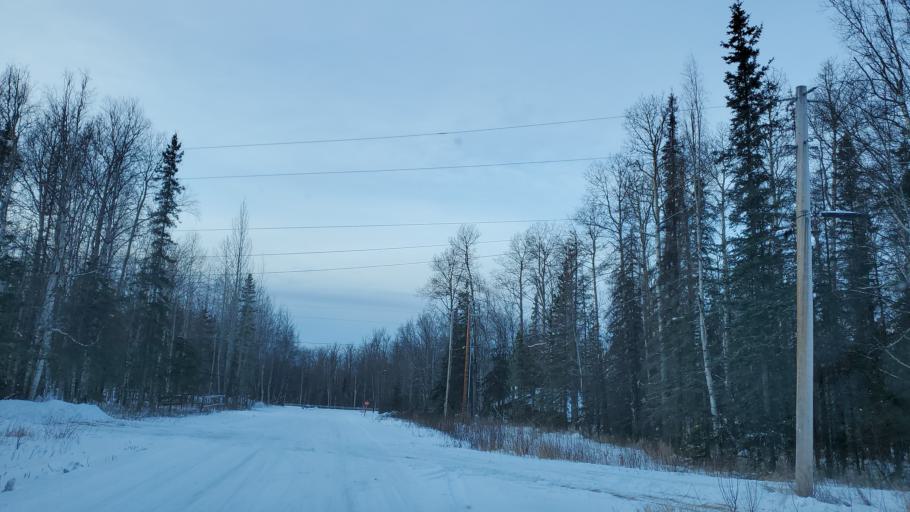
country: US
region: Alaska
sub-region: Matanuska-Susitna Borough
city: Lakes
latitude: 61.6716
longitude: -149.2833
